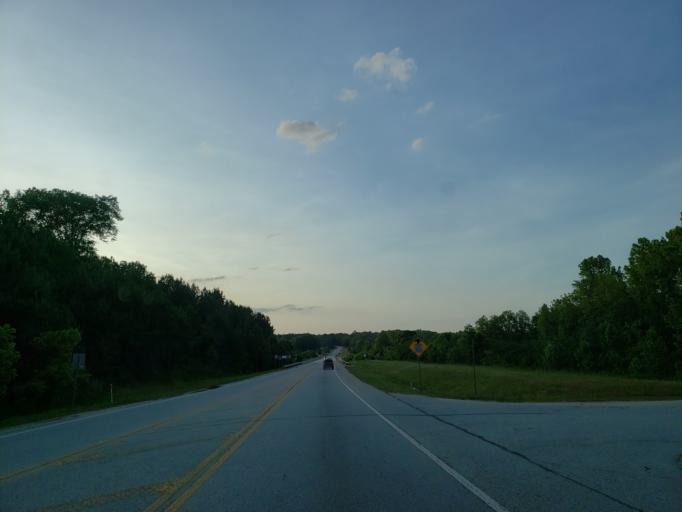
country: US
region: Georgia
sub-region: Coweta County
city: Newnan
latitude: 33.4740
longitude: -84.8997
